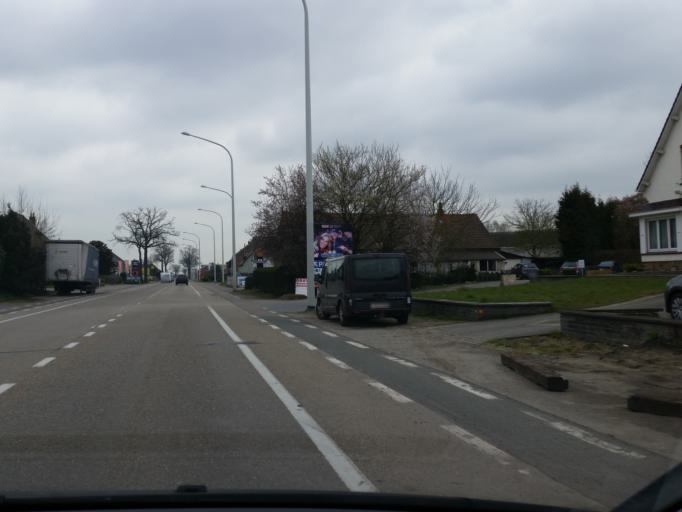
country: BE
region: Flanders
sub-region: Provincie Vlaams-Brabant
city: Boortmeerbeek
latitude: 50.9708
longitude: 4.5694
